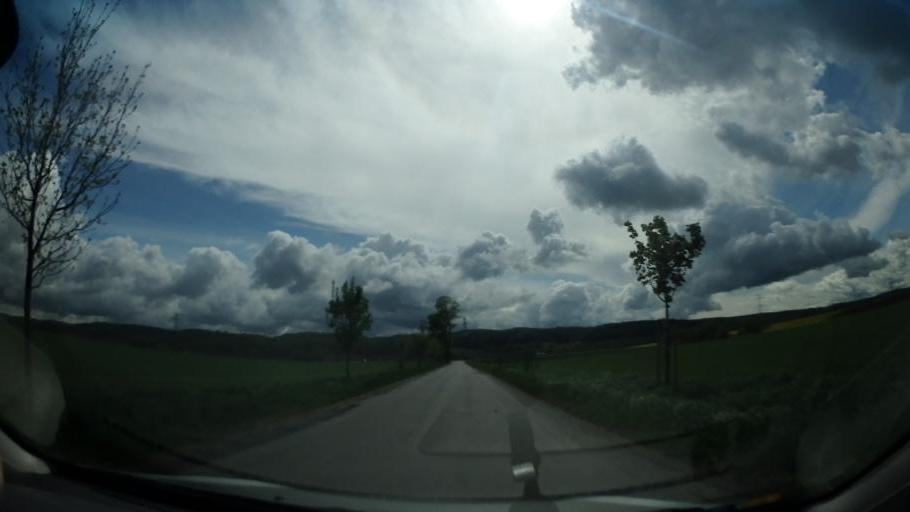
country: CZ
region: South Moravian
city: Ricany
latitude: 49.2285
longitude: 16.4156
